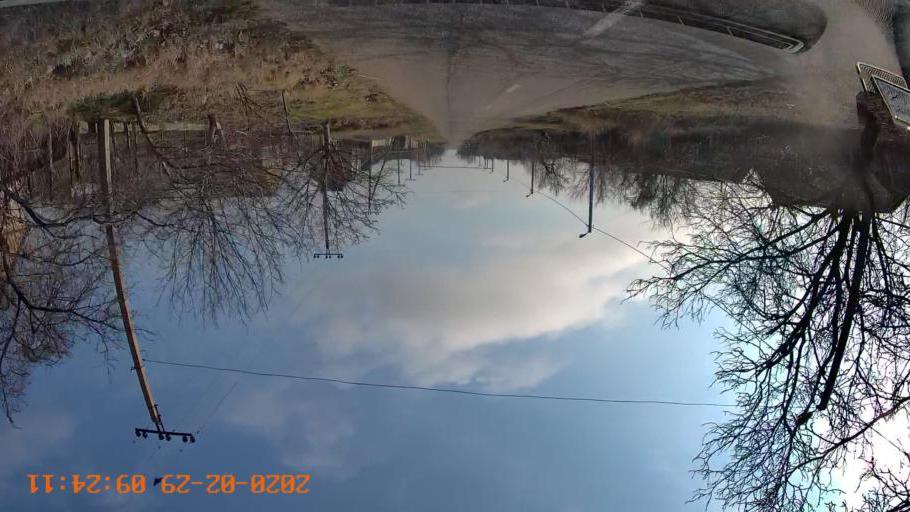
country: MD
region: Telenesti
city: Pervomaisc
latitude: 46.7187
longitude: 29.9593
